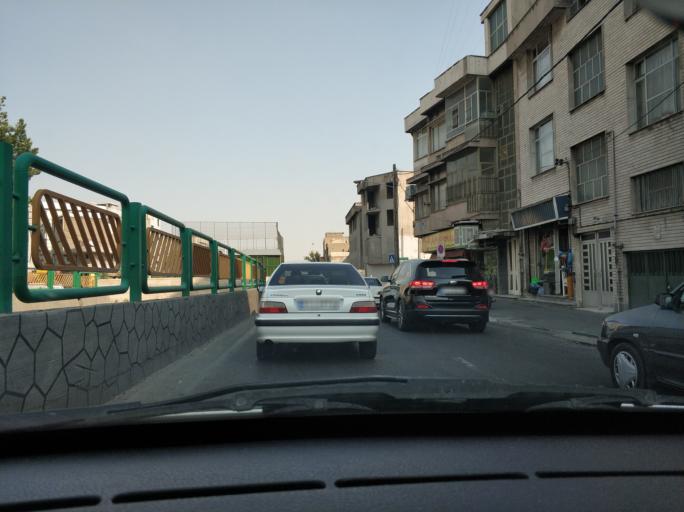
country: IR
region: Tehran
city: Tehran
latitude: 35.7336
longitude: 51.4609
